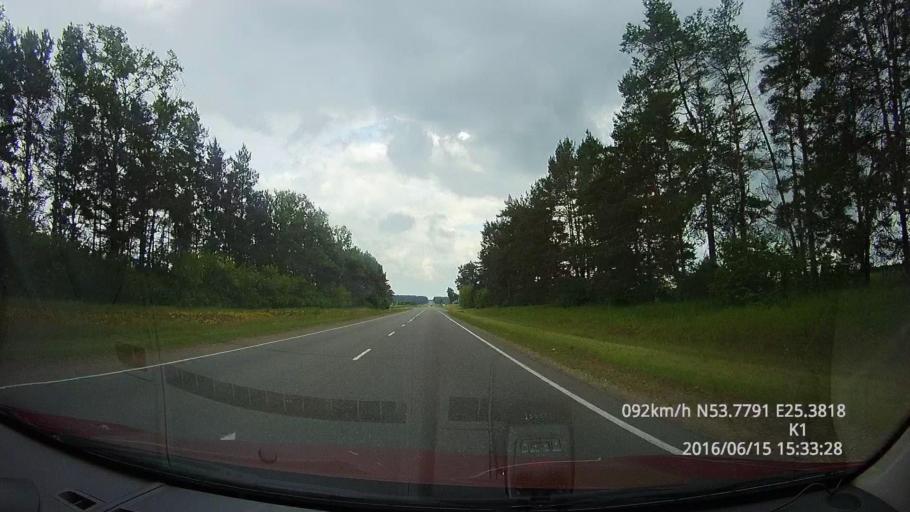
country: BY
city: Berezovka
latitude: 53.7783
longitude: 25.3822
